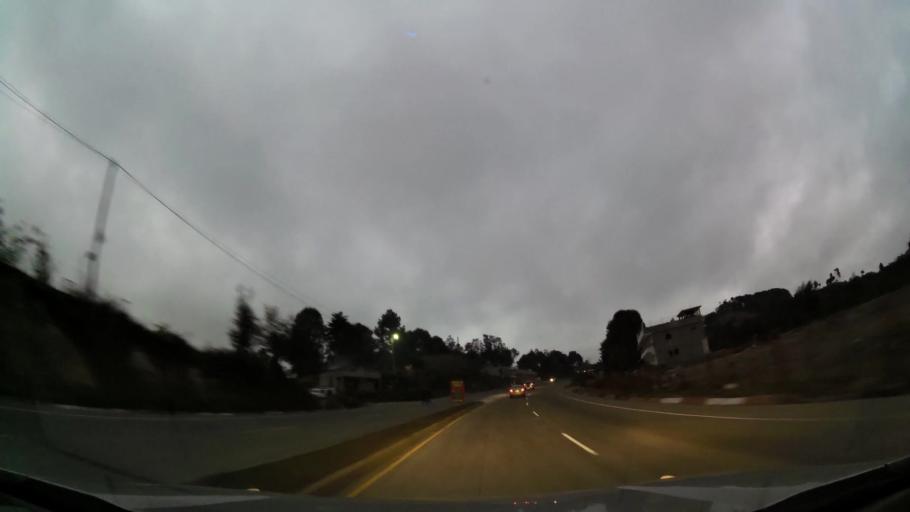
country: GT
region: Chimaltenango
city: Santa Apolonia
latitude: 14.8259
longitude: -91.0185
